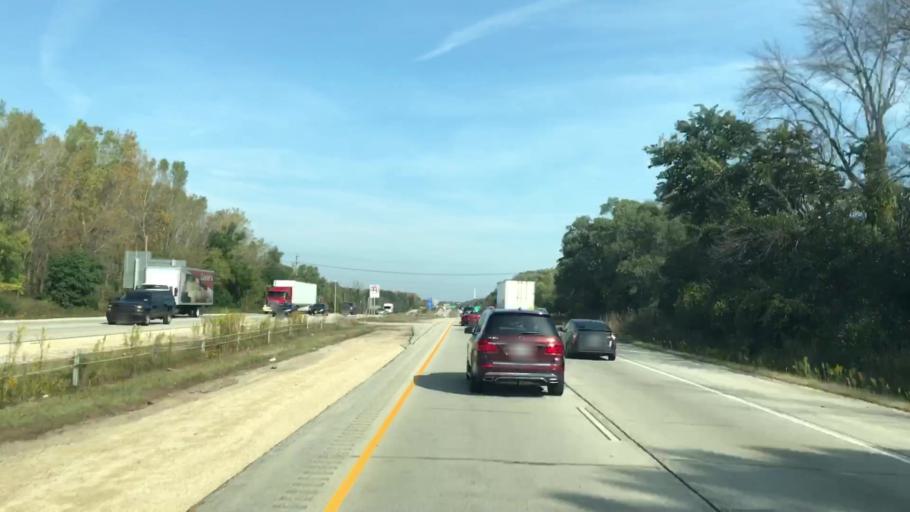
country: US
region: Wisconsin
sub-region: Milwaukee County
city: Fox Point
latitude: 43.1607
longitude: -87.9158
